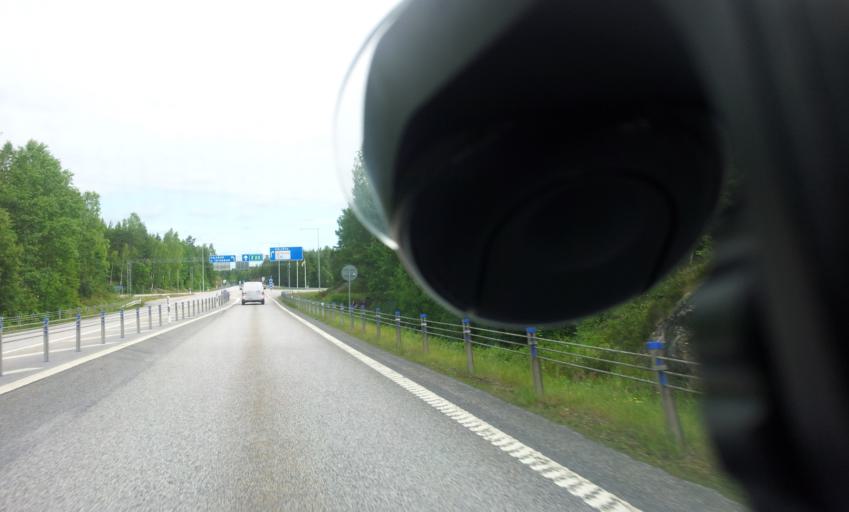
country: SE
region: OEstergoetland
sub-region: Valdemarsviks Kommun
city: Valdemarsvik
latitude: 58.1577
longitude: 16.5434
